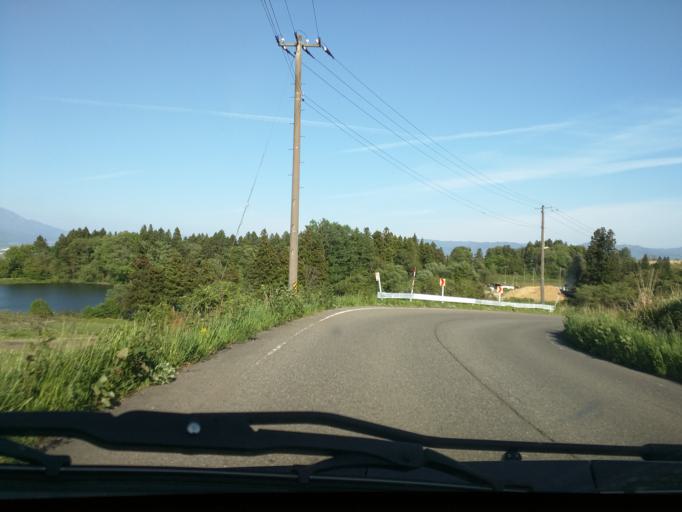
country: JP
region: Fukushima
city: Kitakata
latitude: 37.5228
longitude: 139.8016
